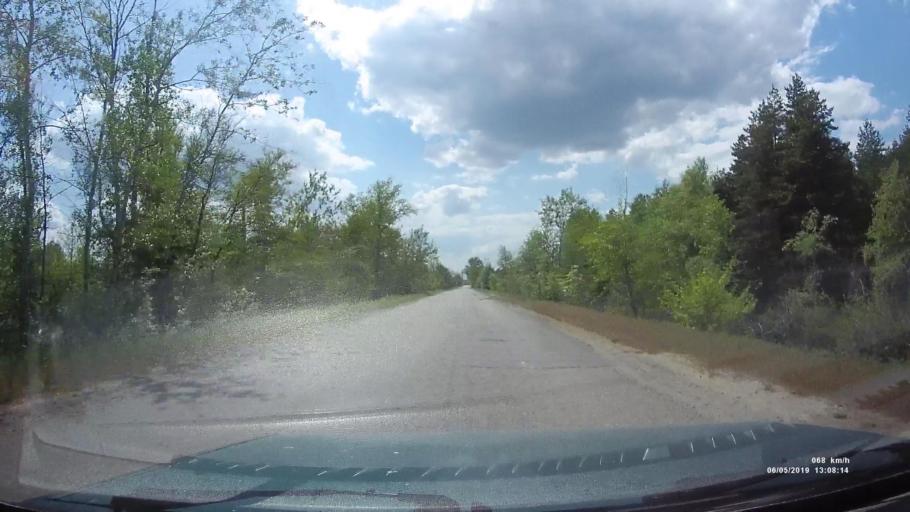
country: RU
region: Rostov
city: Ust'-Donetskiy
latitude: 47.7770
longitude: 40.9976
